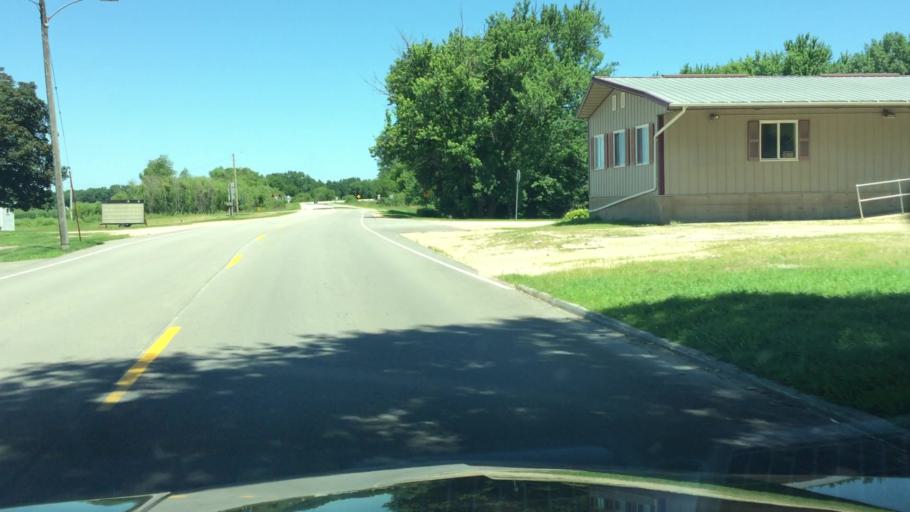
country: US
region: Iowa
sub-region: Cedar County
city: Mechanicsville
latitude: 42.0011
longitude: -91.1419
